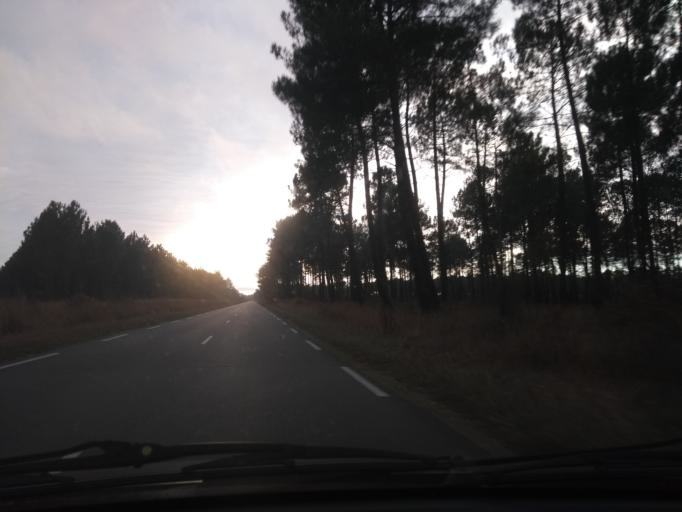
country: FR
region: Aquitaine
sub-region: Departement de la Gironde
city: Le Barp
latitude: 44.6018
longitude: -0.7037
